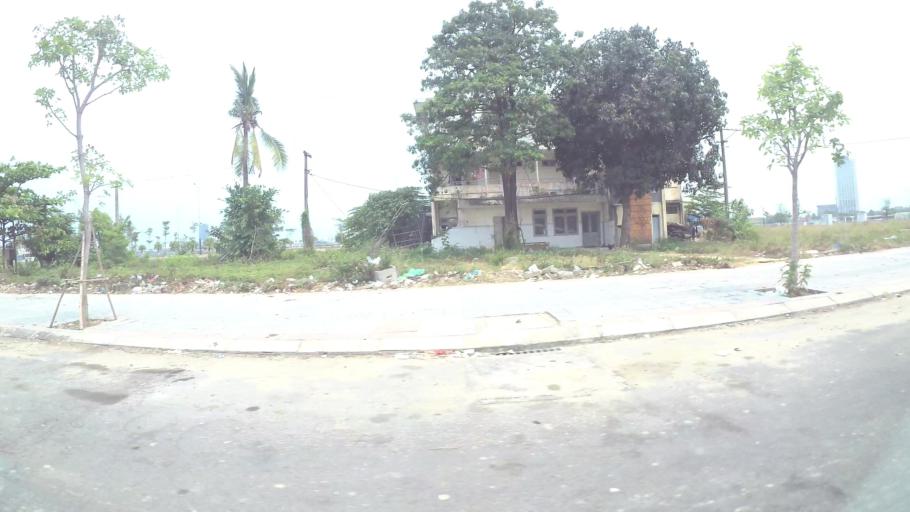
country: VN
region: Da Nang
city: Son Tra
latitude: 16.0535
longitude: 108.2228
